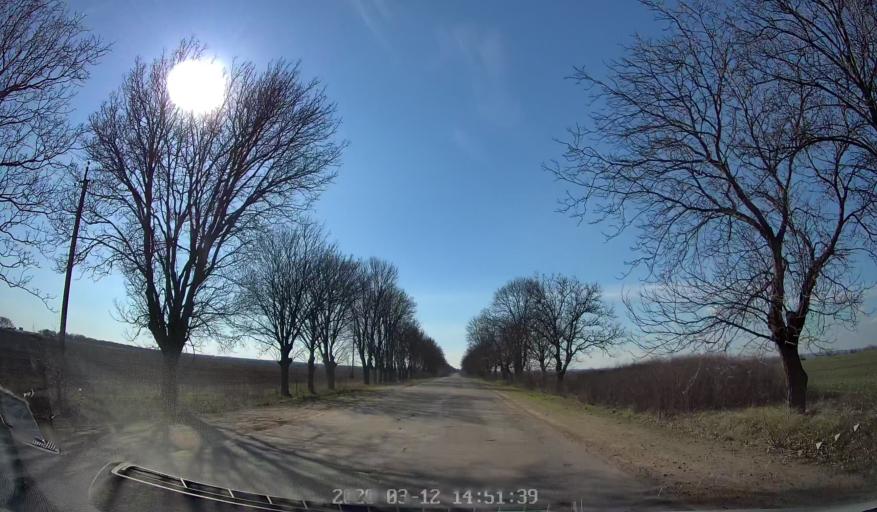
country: MD
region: Criuleni
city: Criuleni
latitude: 47.2218
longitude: 29.1133
